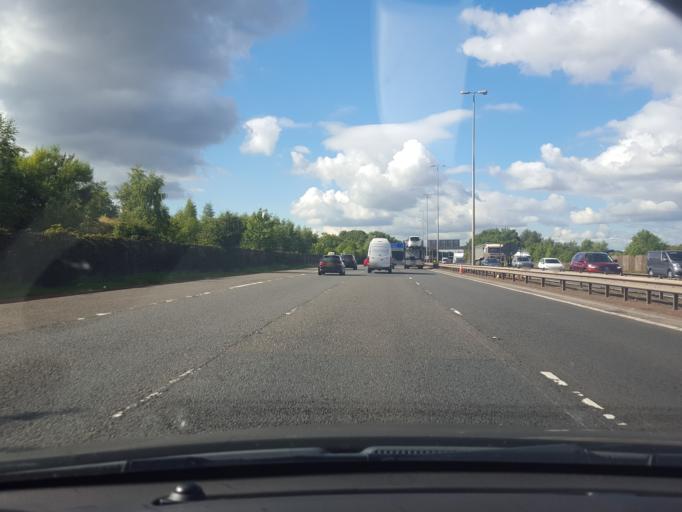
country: GB
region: Scotland
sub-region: South Lanarkshire
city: Uddingston
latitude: 55.8344
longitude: -4.1374
